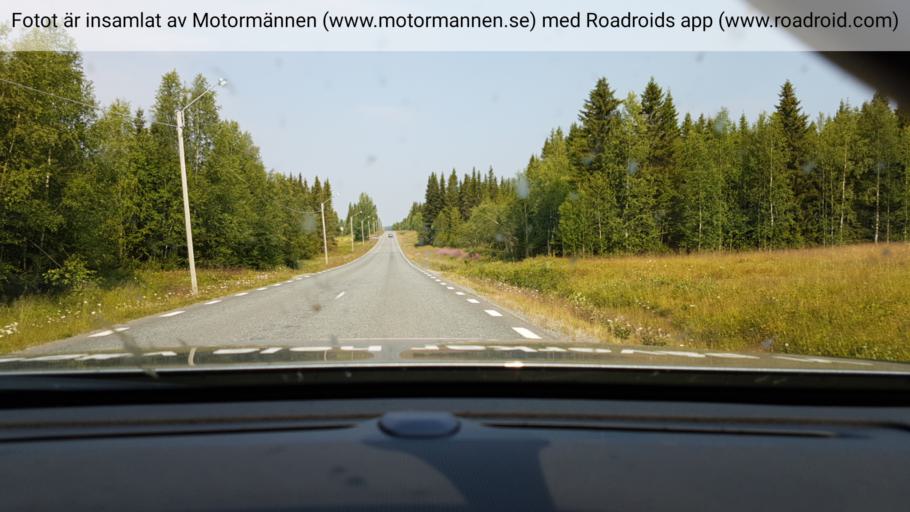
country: SE
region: Vaesterbotten
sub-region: Vilhelmina Kommun
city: Sjoberg
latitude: 65.4546
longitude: 16.0946
